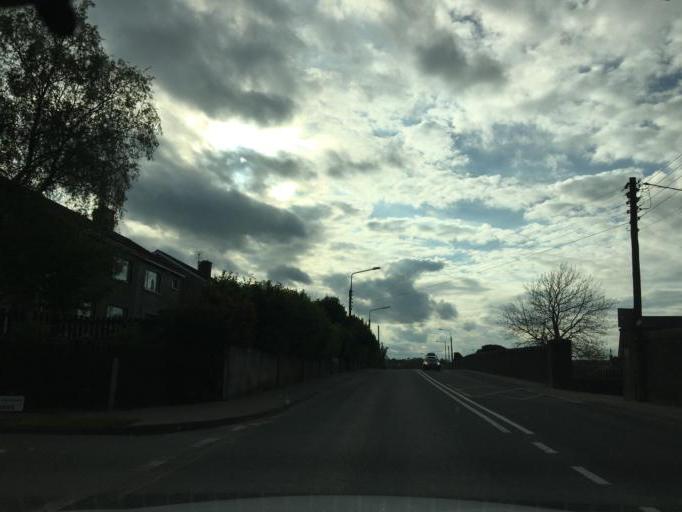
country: IE
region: Leinster
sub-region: Loch Garman
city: Loch Garman
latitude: 52.3406
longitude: -6.4743
